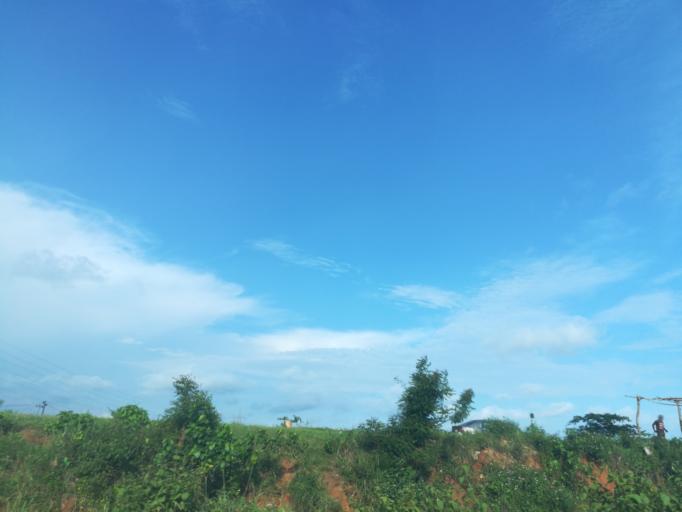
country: NG
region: Ogun
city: Ado Odo
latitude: 6.4975
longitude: 3.0858
